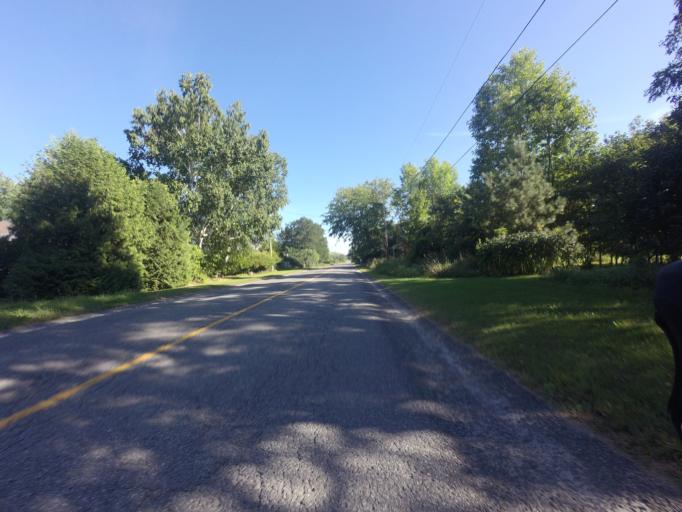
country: CA
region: Ontario
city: Perth
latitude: 44.9187
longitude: -76.3549
